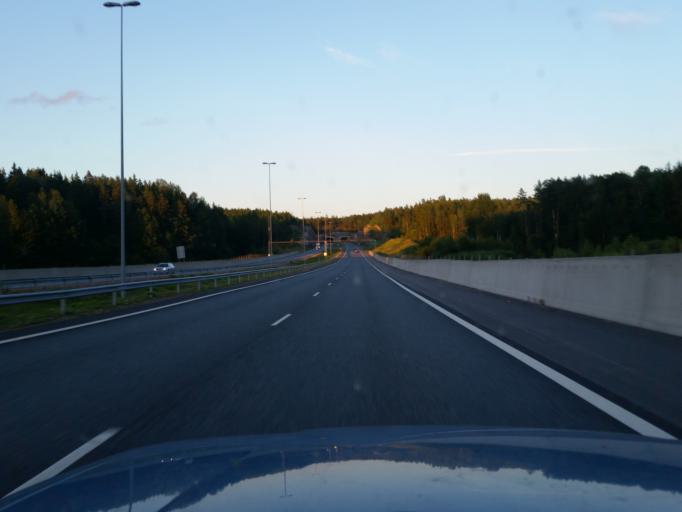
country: FI
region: Varsinais-Suomi
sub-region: Salo
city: Muurla
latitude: 60.3747
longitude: 23.3443
